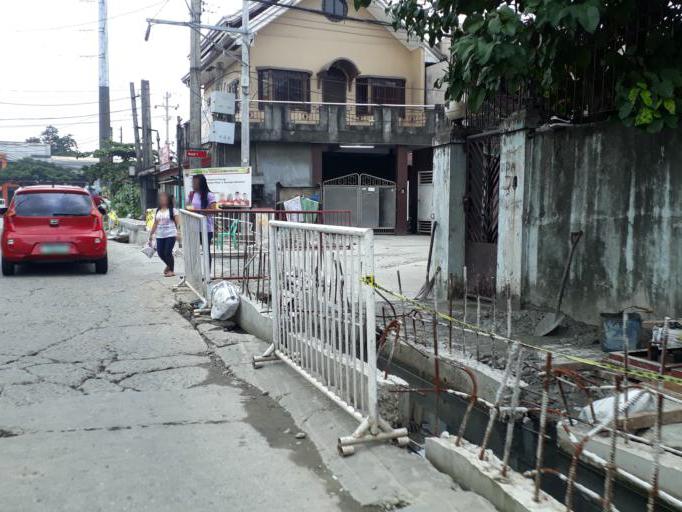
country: PH
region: Calabarzon
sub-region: Province of Rizal
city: Valenzuela
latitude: 14.7067
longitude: 120.9615
